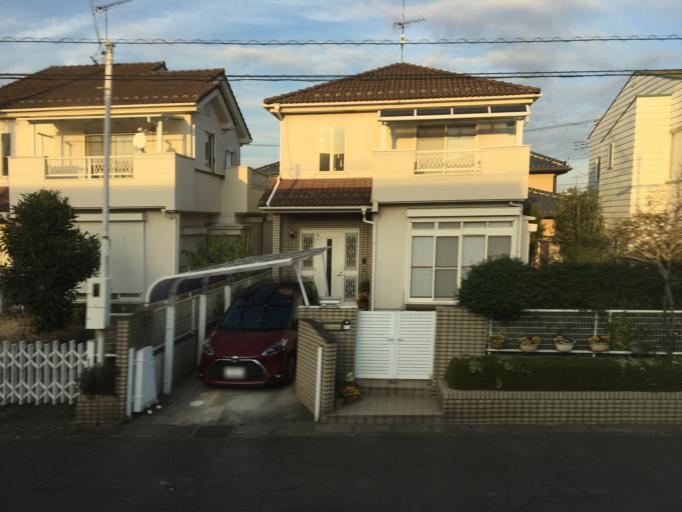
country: JP
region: Saitama
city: Konosu
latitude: 36.0793
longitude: 139.4837
